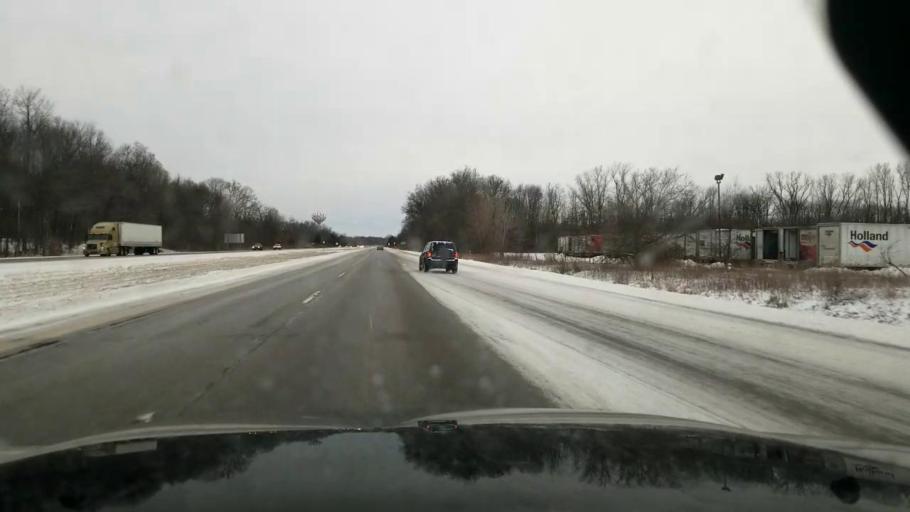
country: US
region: Michigan
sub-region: Jackson County
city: Jackson
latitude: 42.2495
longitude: -84.4762
